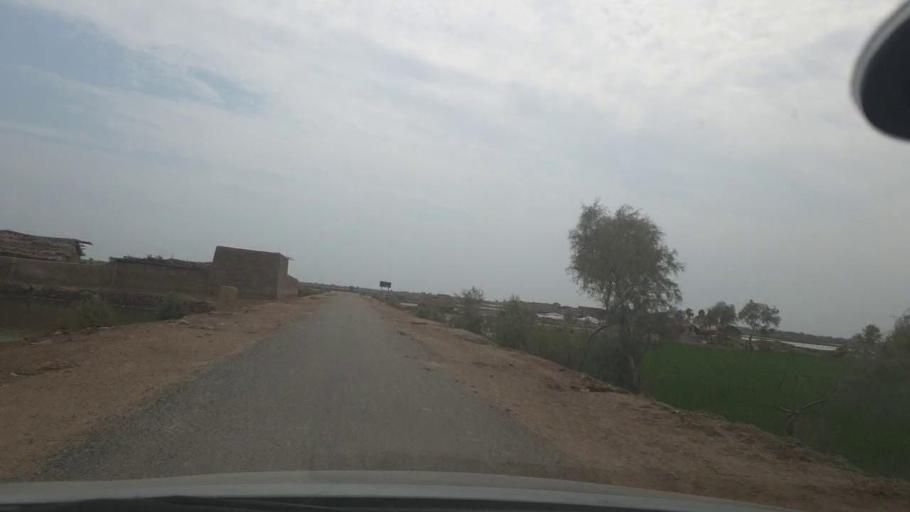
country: PK
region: Balochistan
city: Garhi Khairo
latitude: 28.0172
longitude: 68.0434
